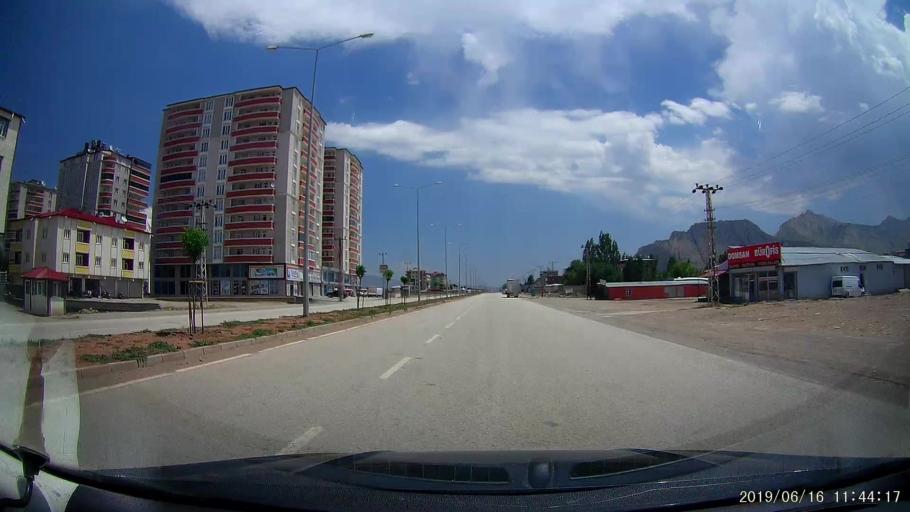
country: TR
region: Agri
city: Dogubayazit
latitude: 39.5572
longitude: 44.0872
